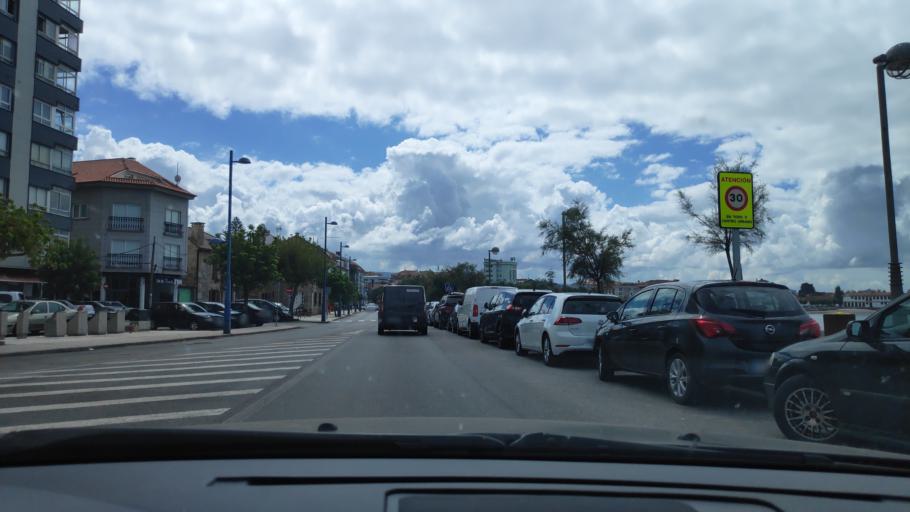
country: ES
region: Galicia
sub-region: Provincia de Pontevedra
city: Cambados
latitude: 42.5189
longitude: -8.8172
